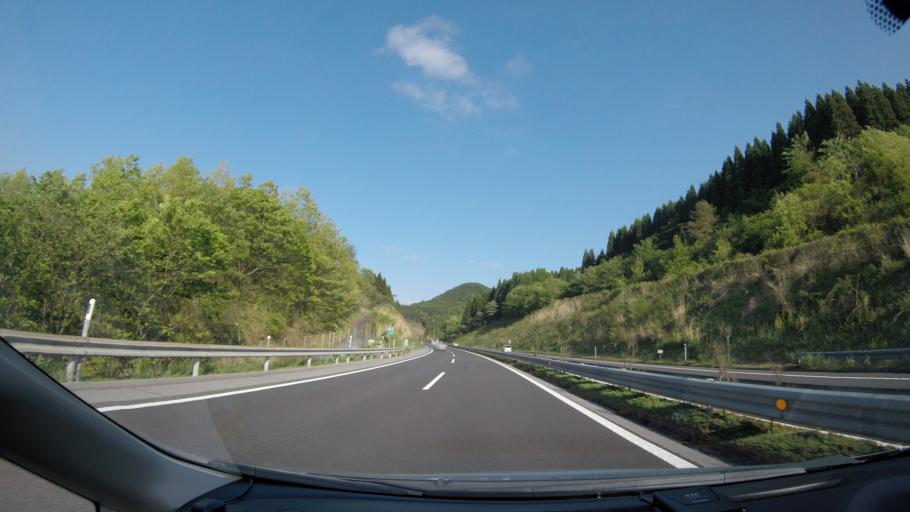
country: JP
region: Oita
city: Tsukawaki
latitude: 33.2523
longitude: 131.2758
